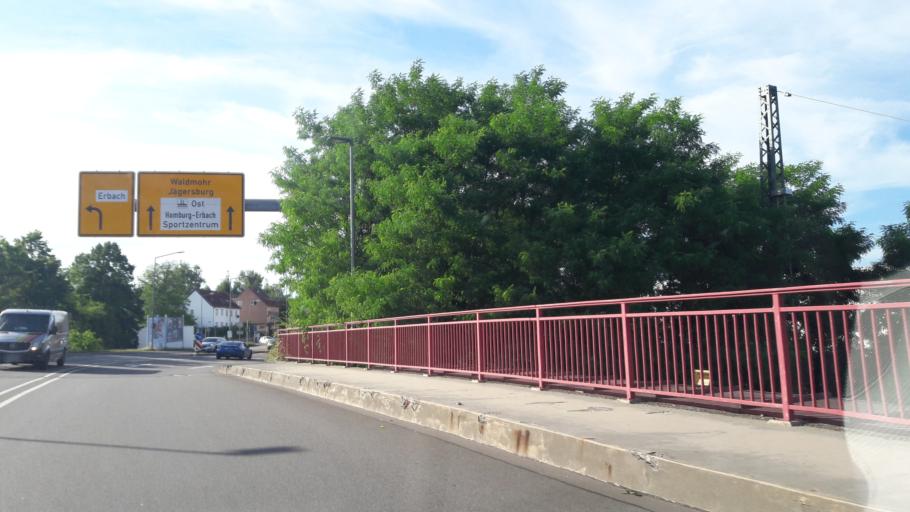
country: DE
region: Saarland
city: Homburg
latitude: 49.3294
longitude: 7.3385
